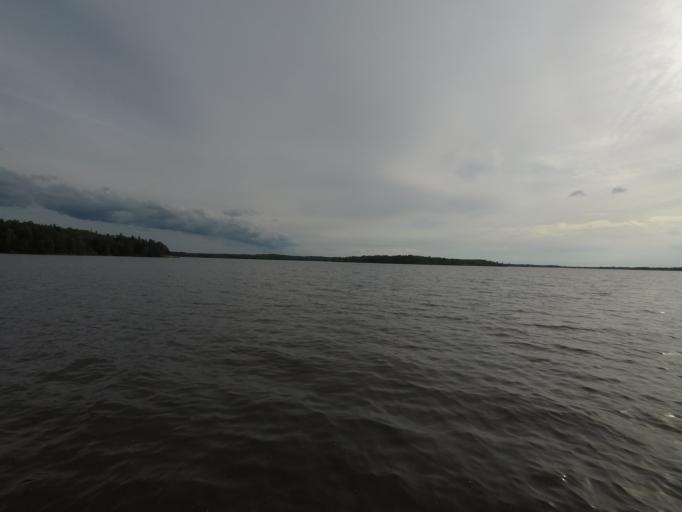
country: SE
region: Soedermanland
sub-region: Eskilstuna Kommun
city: Kvicksund
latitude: 59.4726
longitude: 16.3929
